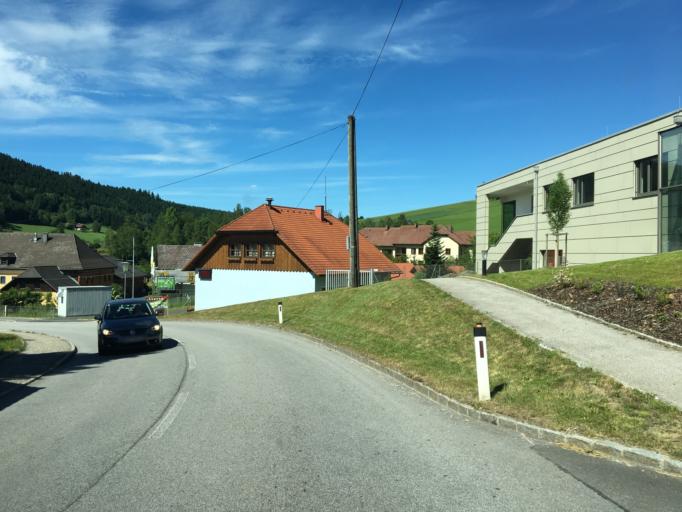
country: AT
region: Upper Austria
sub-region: Politischer Bezirk Urfahr-Umgebung
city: Eidenberg
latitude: 48.4256
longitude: 14.2382
